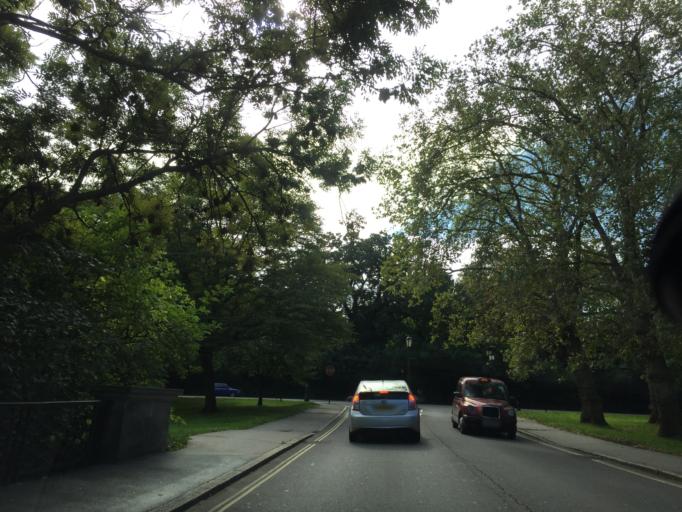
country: GB
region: England
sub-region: Greater London
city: Belsize Park
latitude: 51.5345
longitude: -0.1632
